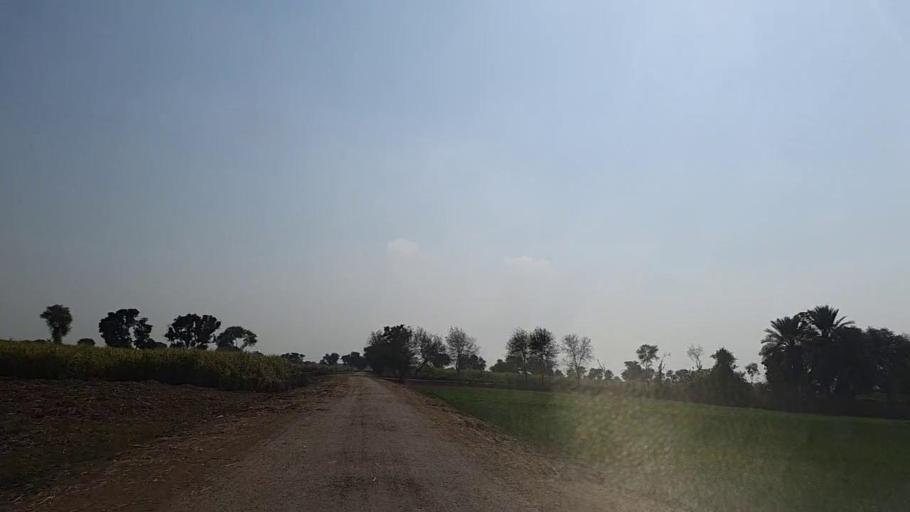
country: PK
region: Sindh
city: Daur
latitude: 26.4384
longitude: 68.2332
